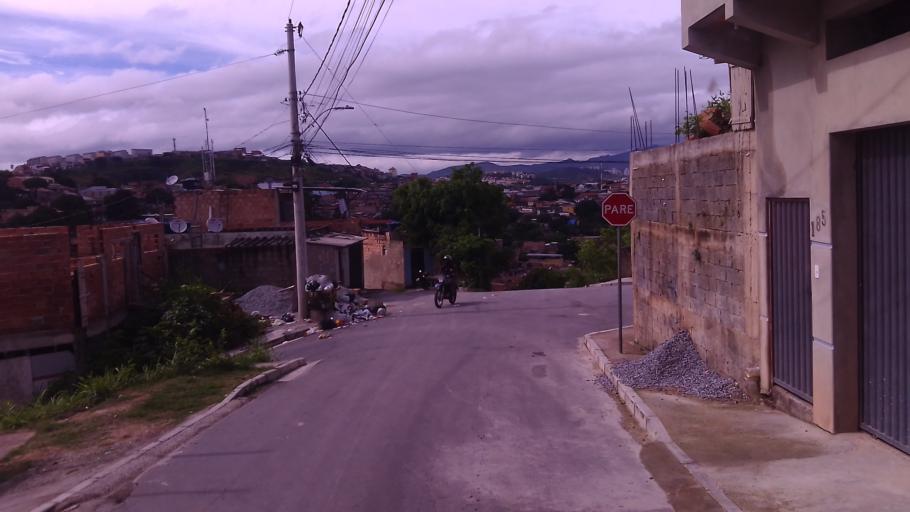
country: BR
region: Minas Gerais
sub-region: Santa Luzia
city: Santa Luzia
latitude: -19.8380
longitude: -43.8983
